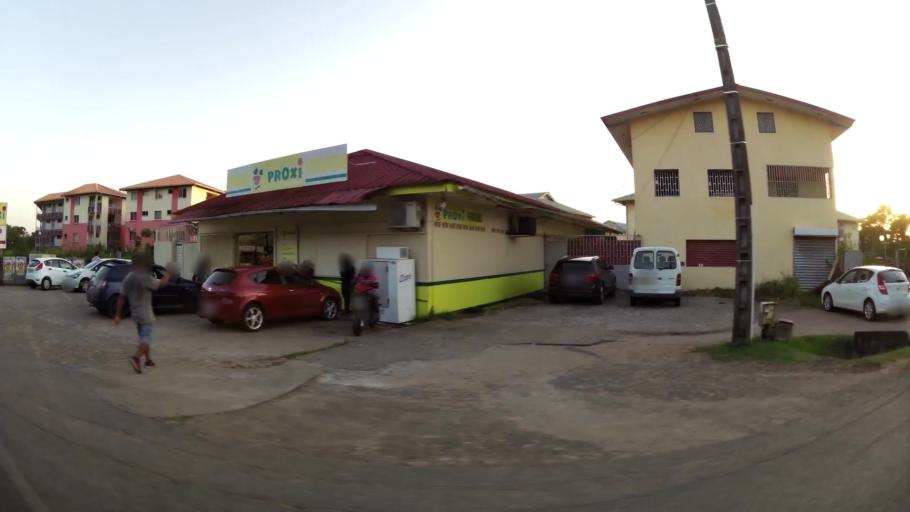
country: GF
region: Guyane
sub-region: Guyane
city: Cayenne
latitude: 4.9255
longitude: -52.3128
